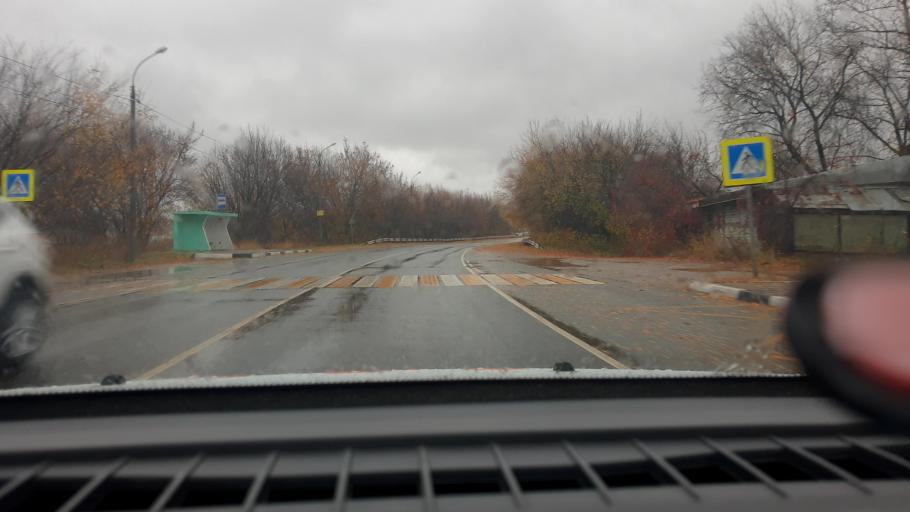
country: RU
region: Nizjnij Novgorod
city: Kstovo
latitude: 56.1369
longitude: 44.1806
